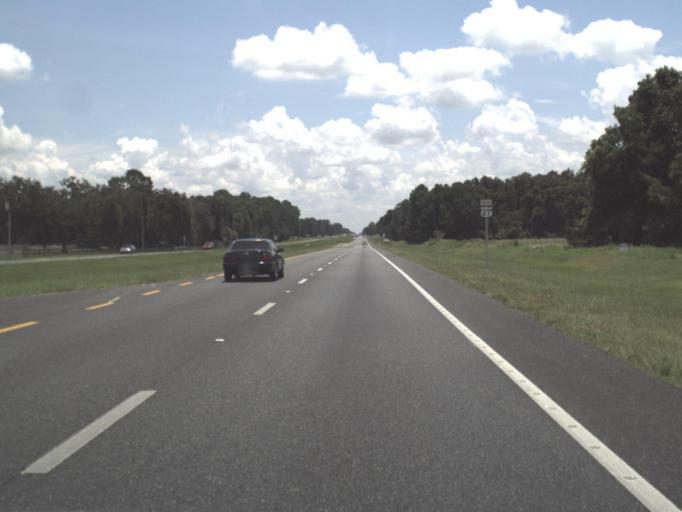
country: US
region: Florida
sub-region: Levy County
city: Williston
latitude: 29.3735
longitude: -82.4163
